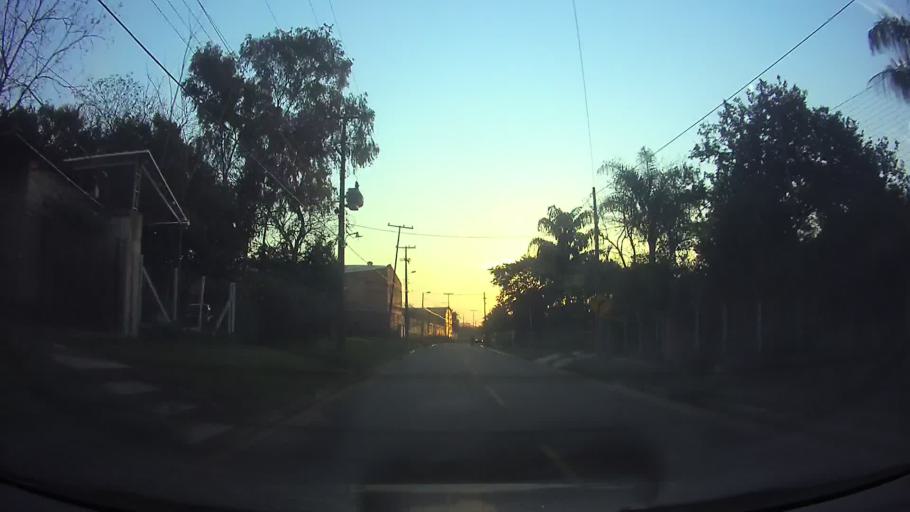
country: PY
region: Central
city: Limpio
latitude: -25.2377
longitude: -57.5018
